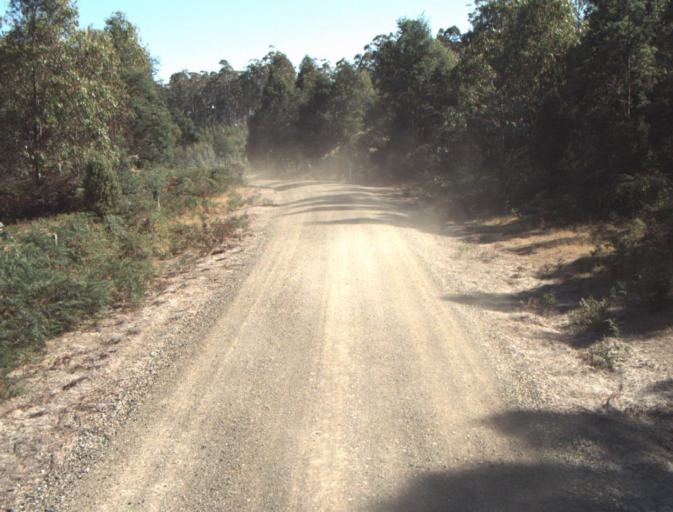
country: AU
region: Tasmania
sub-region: Dorset
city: Scottsdale
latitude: -41.2706
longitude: 147.3764
